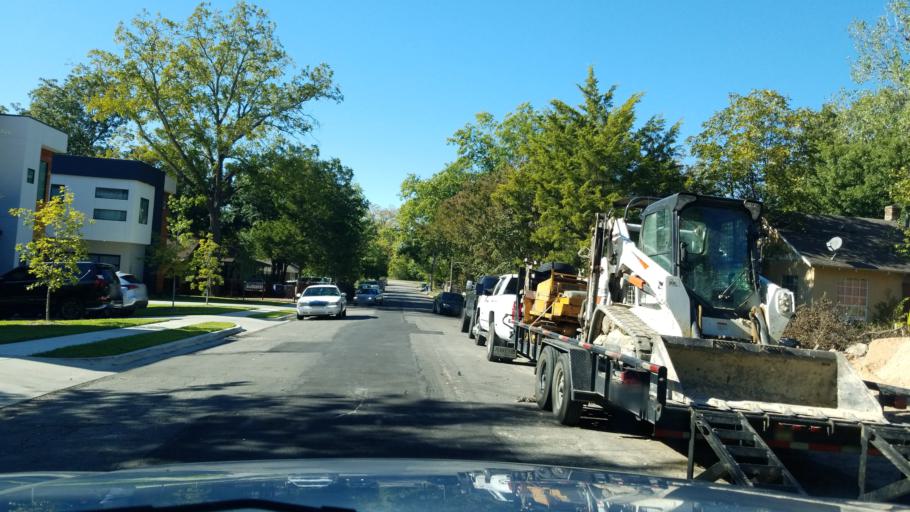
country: US
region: Texas
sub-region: Dallas County
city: Highland Park
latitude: 32.8036
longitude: -96.7463
